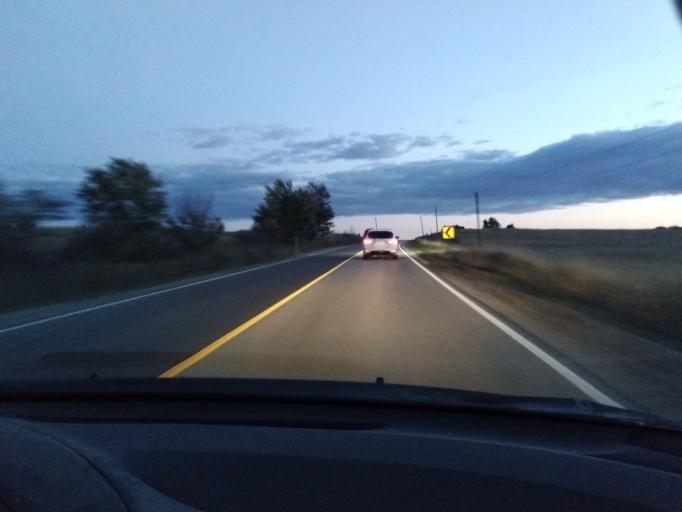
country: CA
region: Ontario
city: Bradford West Gwillimbury
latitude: 44.1038
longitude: -79.6405
